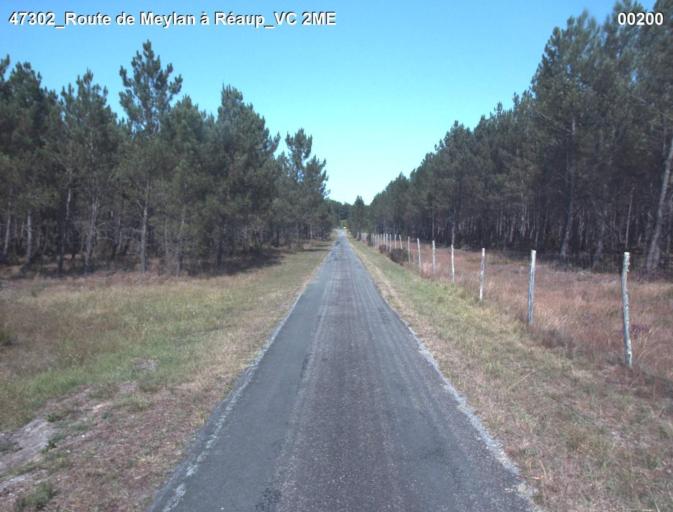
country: FR
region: Aquitaine
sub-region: Departement du Lot-et-Garonne
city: Mezin
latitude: 44.1061
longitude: 0.1397
